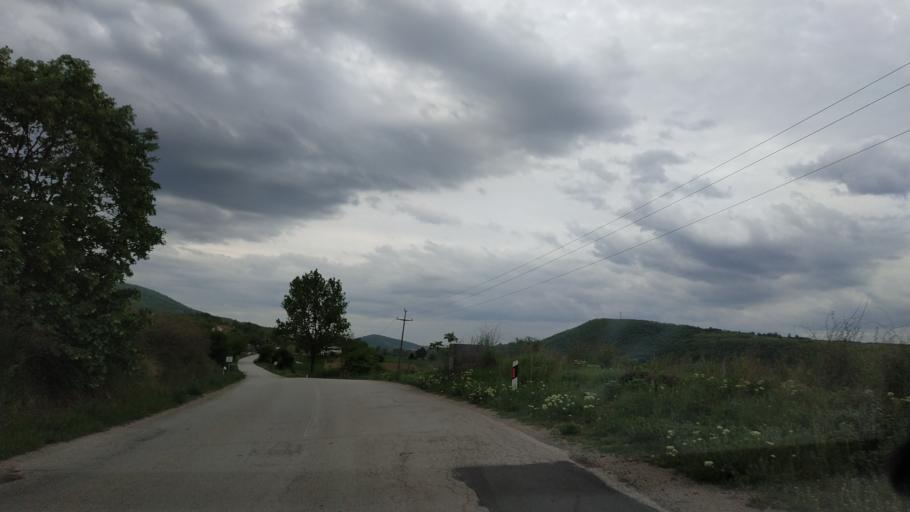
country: RS
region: Central Serbia
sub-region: Nisavski Okrug
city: Aleksinac
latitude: 43.5994
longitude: 21.6871
